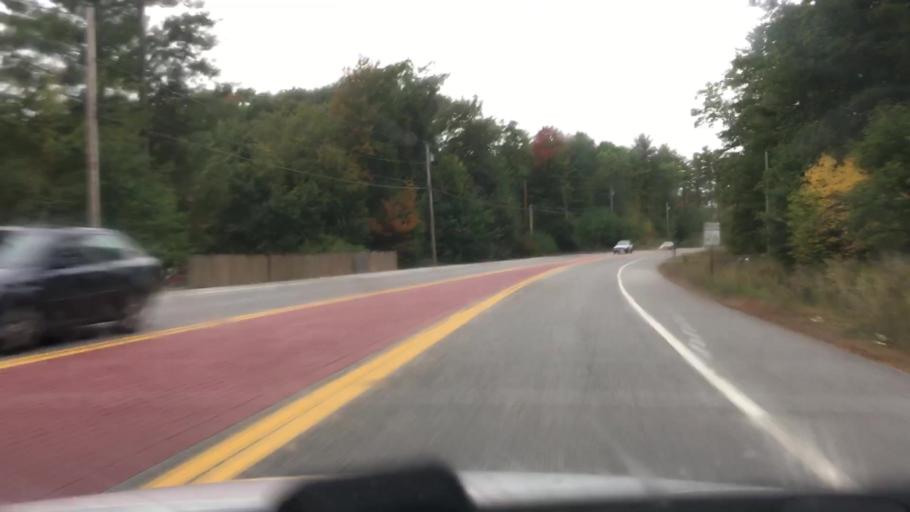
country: US
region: Maine
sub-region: Androscoggin County
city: Poland
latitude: 44.0389
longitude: -70.3756
